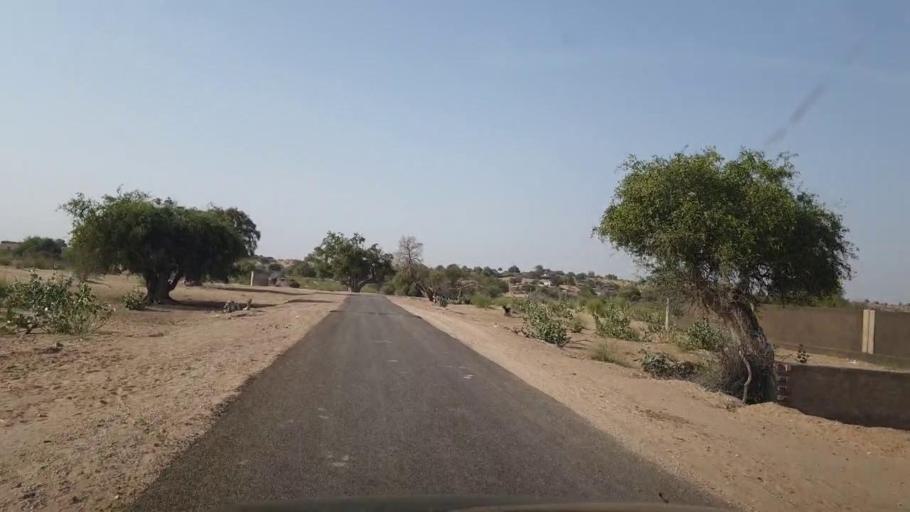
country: PK
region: Sindh
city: Islamkot
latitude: 25.1623
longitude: 70.5224
